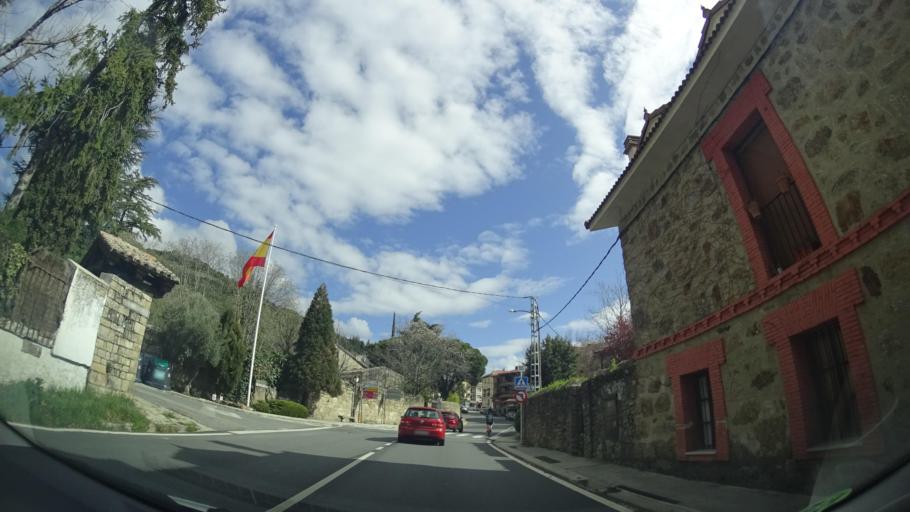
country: ES
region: Madrid
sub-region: Provincia de Madrid
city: Miraflores de la Sierra
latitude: 40.8119
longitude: -3.7690
